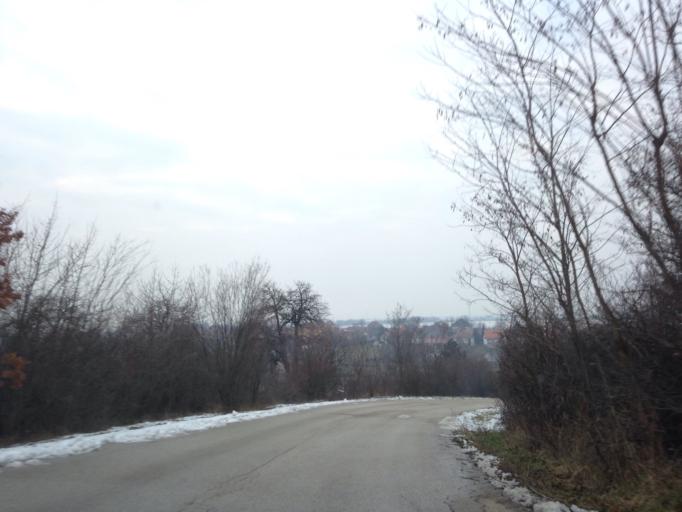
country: SK
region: Nitriansky
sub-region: Okres Nitra
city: Vrable
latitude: 48.1016
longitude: 18.3541
